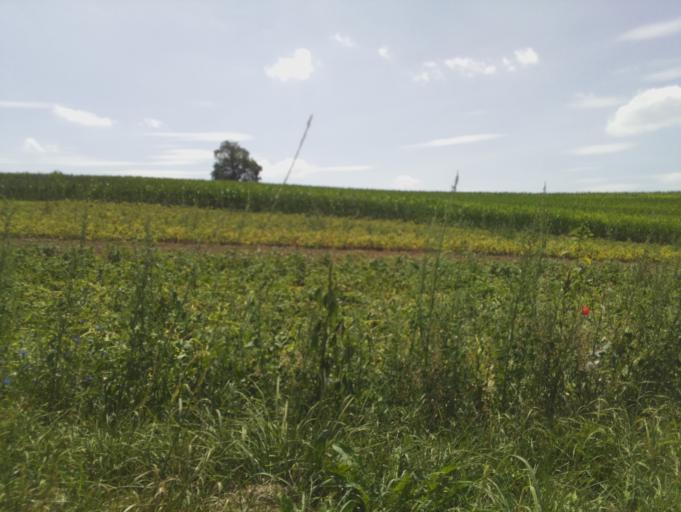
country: CH
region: Zurich
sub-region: Bezirk Andelfingen
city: Kleinandelfingen
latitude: 47.6181
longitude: 8.7189
